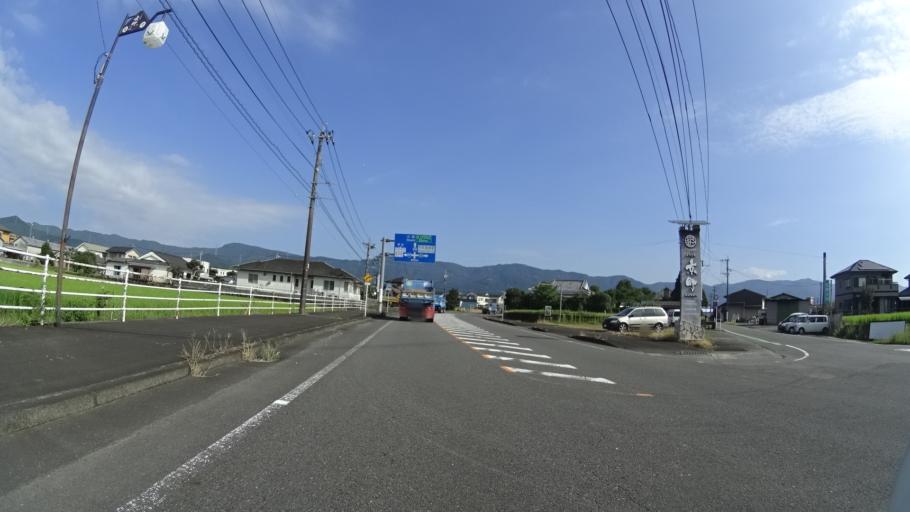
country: JP
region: Kagoshima
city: Okuchi-shinohara
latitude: 32.0431
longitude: 130.7629
